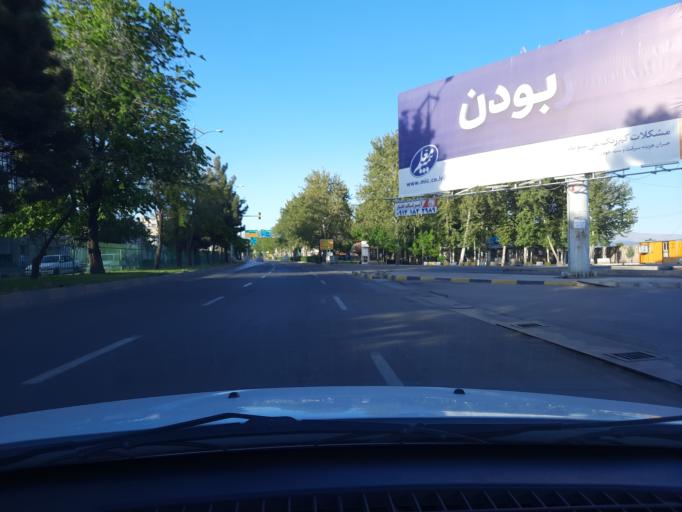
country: IR
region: Qazvin
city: Qazvin
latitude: 36.2698
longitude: 50.0213
